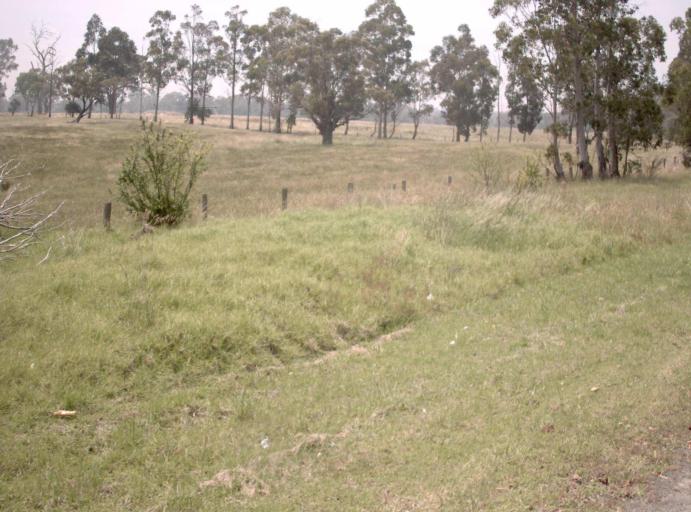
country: AU
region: Victoria
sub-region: Latrobe
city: Traralgon
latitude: -38.2494
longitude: 146.6541
